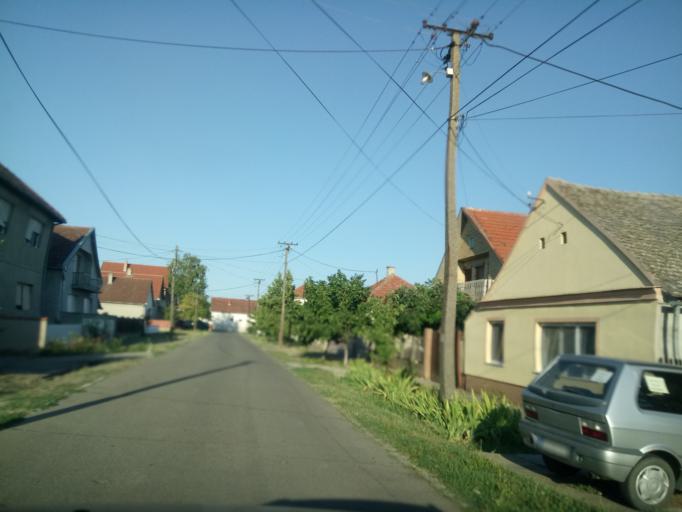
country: RS
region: Autonomna Pokrajina Vojvodina
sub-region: Sremski Okrug
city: Stara Pazova
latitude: 44.9897
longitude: 20.1709
